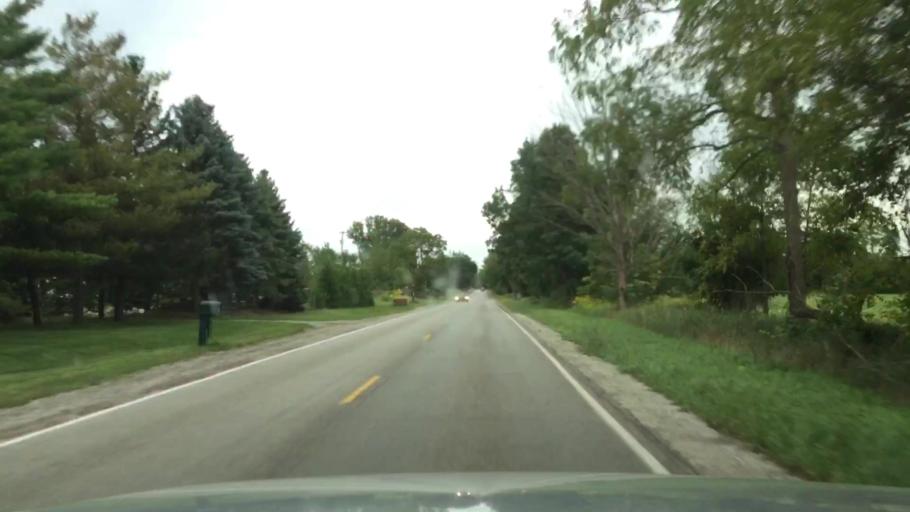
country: US
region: Michigan
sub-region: Genesee County
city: Argentine
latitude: 42.8050
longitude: -83.8770
